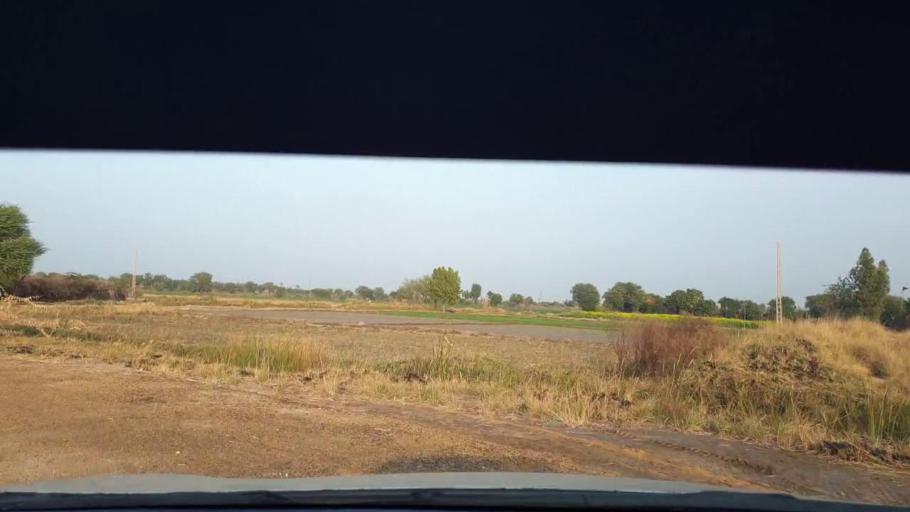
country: PK
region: Sindh
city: Berani
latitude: 25.7242
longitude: 68.9779
